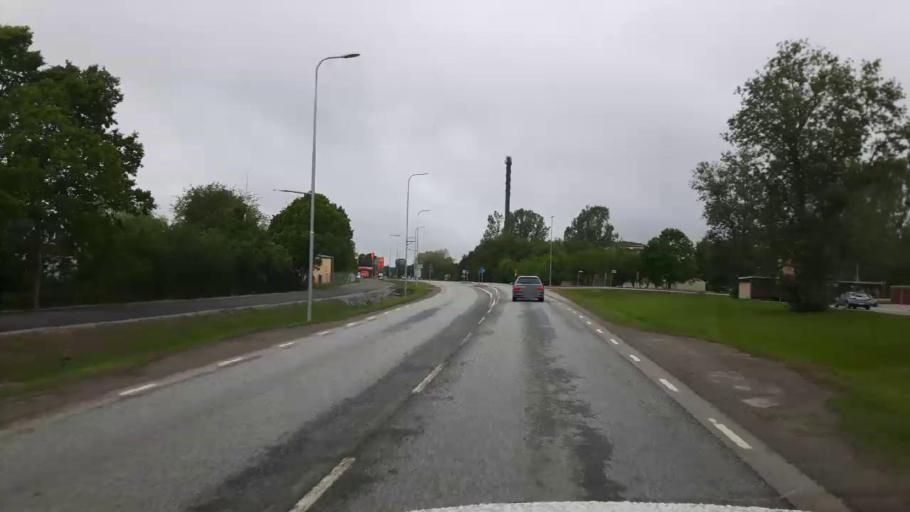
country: SE
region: Stockholm
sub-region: Upplands-Bro Kommun
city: Bro
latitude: 59.5133
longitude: 17.6463
